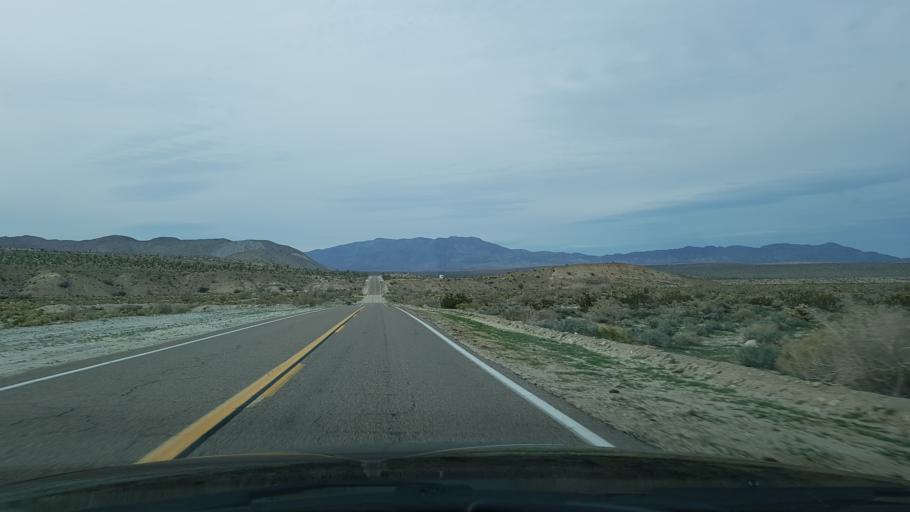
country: US
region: California
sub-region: San Diego County
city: Pine Valley
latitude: 32.8447
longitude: -116.1989
